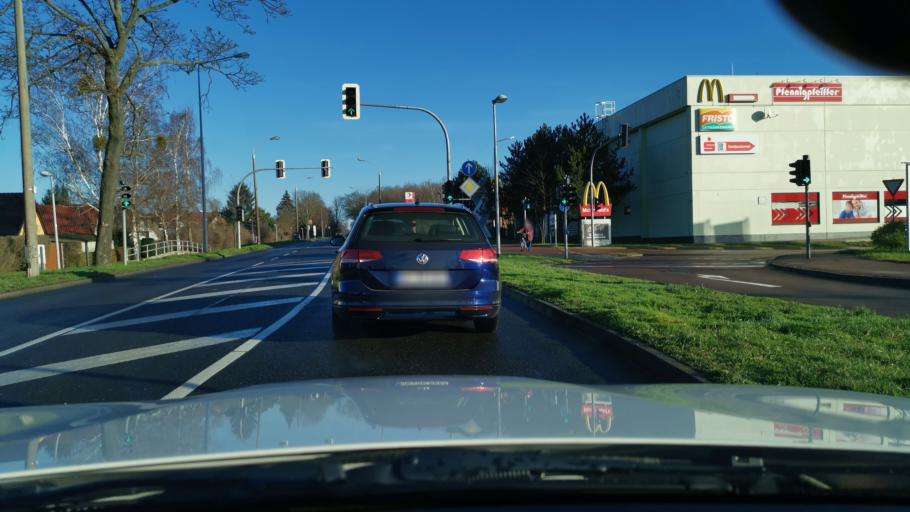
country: DE
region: Saxony-Anhalt
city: Wittenburg
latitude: 51.8895
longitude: 12.6637
